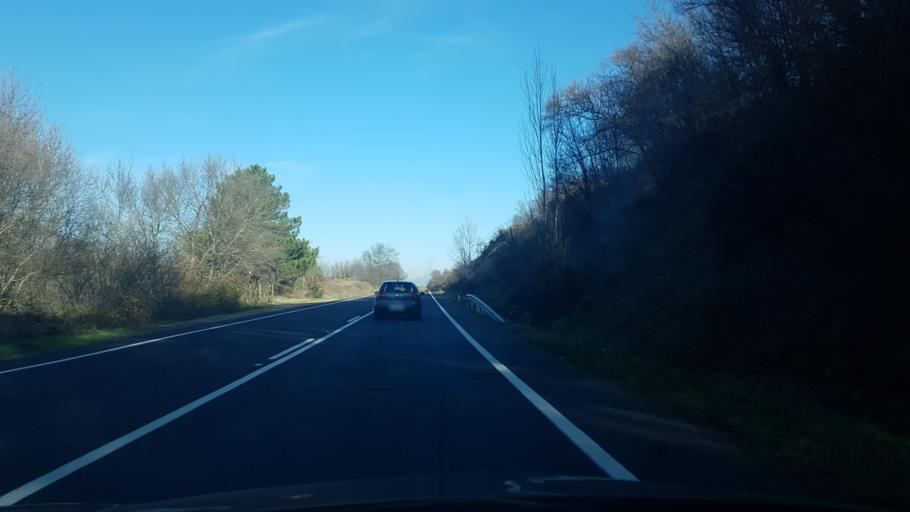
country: ES
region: Castille and Leon
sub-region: Provincia de Avila
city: Navahondilla
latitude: 40.3162
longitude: -4.4967
